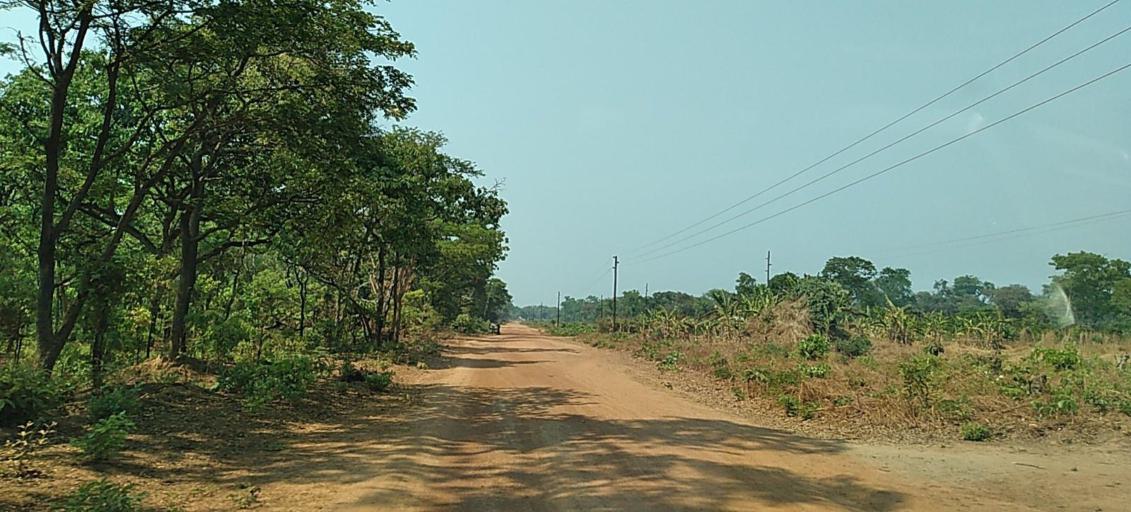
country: ZM
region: Copperbelt
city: Kalulushi
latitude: -13.1000
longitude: 27.4046
